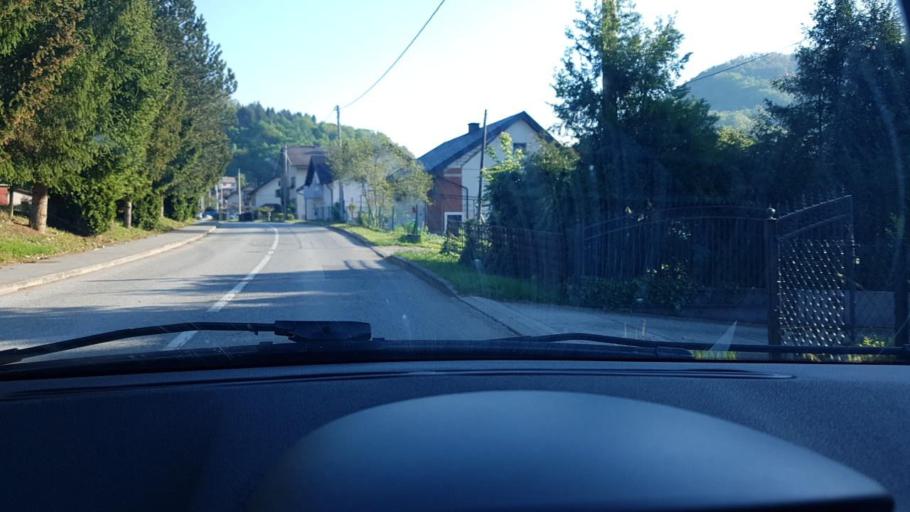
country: HR
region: Krapinsko-Zagorska
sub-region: Grad Krapina
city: Krapina
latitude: 46.1992
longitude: 15.8415
